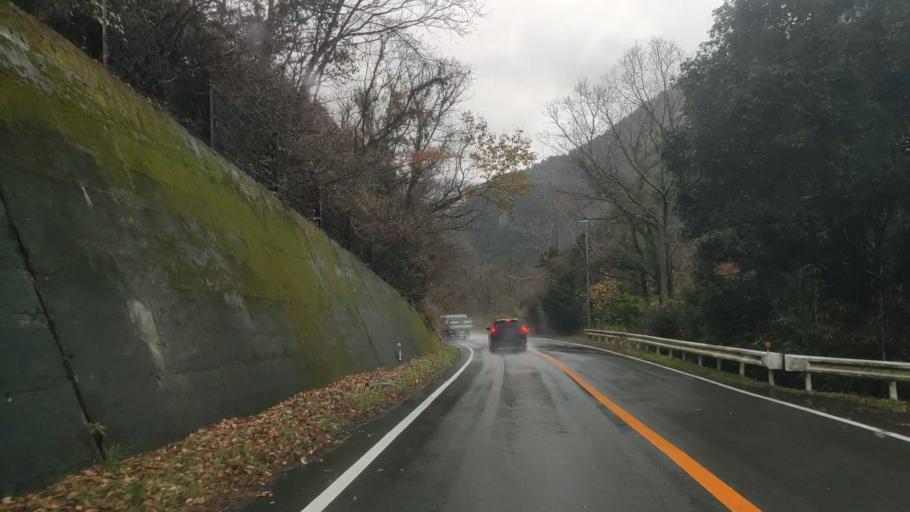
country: JP
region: Tokushima
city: Kamojimacho-jogejima
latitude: 34.1651
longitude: 134.3463
